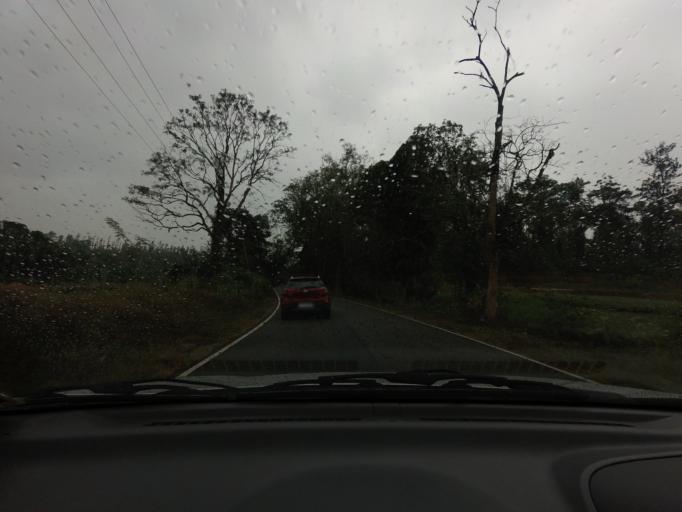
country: IN
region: Karnataka
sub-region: Hassan
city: Sakleshpur
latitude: 12.9731
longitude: 75.7194
